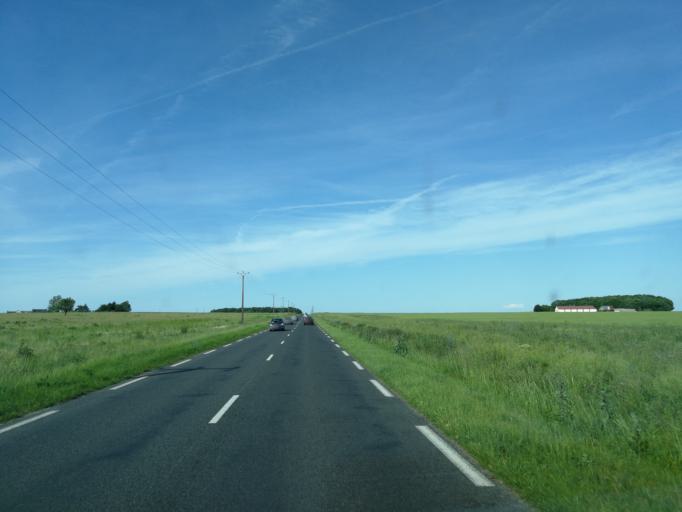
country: FR
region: Centre
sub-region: Departement d'Indre-et-Loire
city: Monnaie
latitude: 47.5173
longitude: 0.8152
